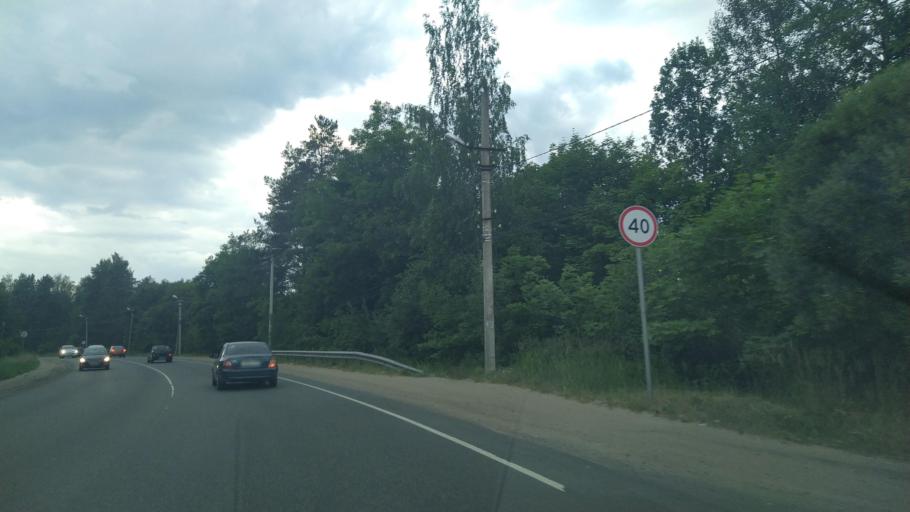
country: RU
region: Leningrad
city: Toksovo
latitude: 60.1547
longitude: 30.5246
